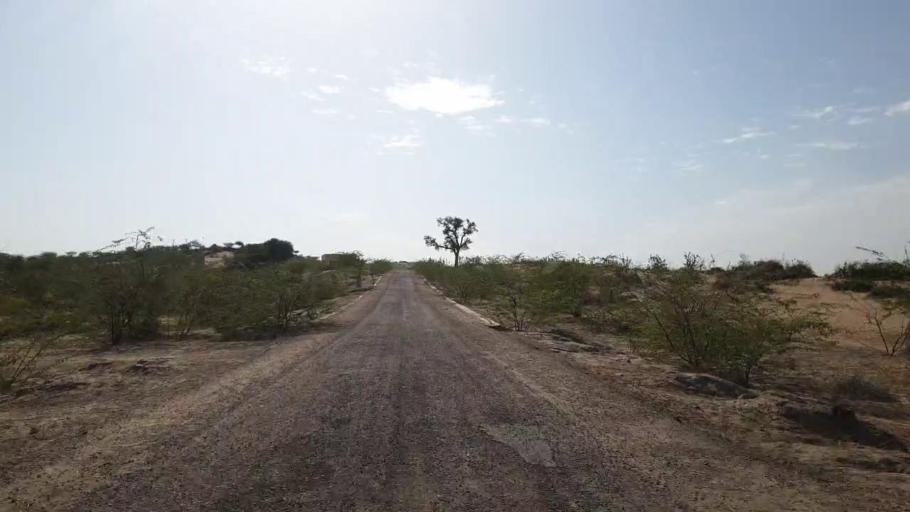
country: PK
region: Sindh
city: Islamkot
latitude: 25.0646
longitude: 70.0392
